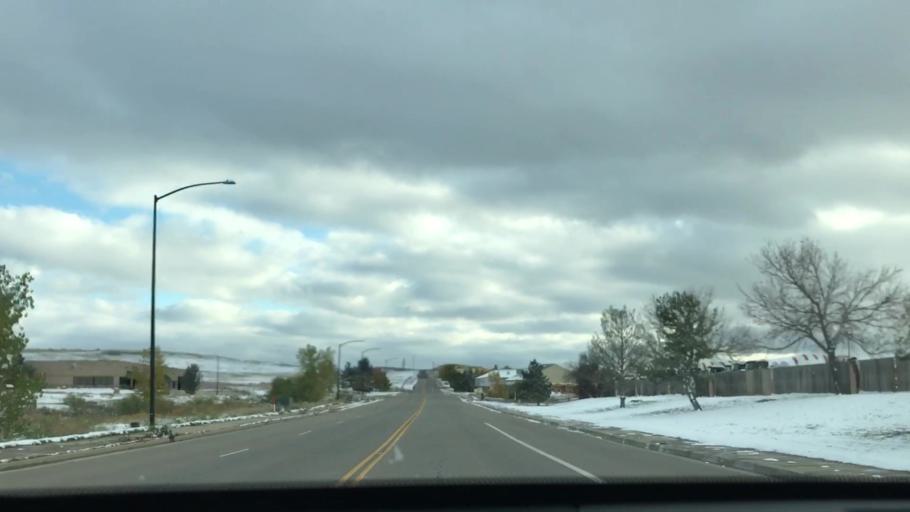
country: US
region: Colorado
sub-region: Boulder County
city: Lafayette
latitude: 39.9790
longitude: -105.0719
